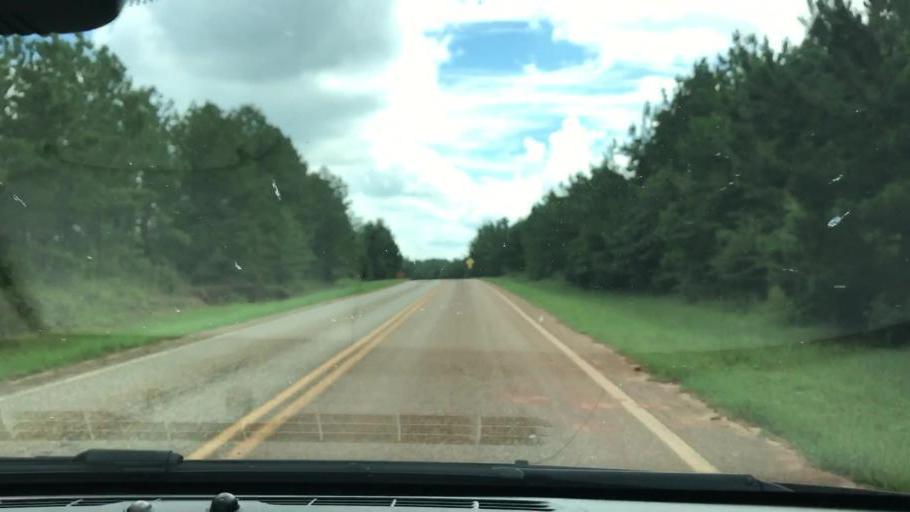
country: US
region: Georgia
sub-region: Stewart County
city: Lumpkin
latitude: 32.0731
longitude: -84.8724
